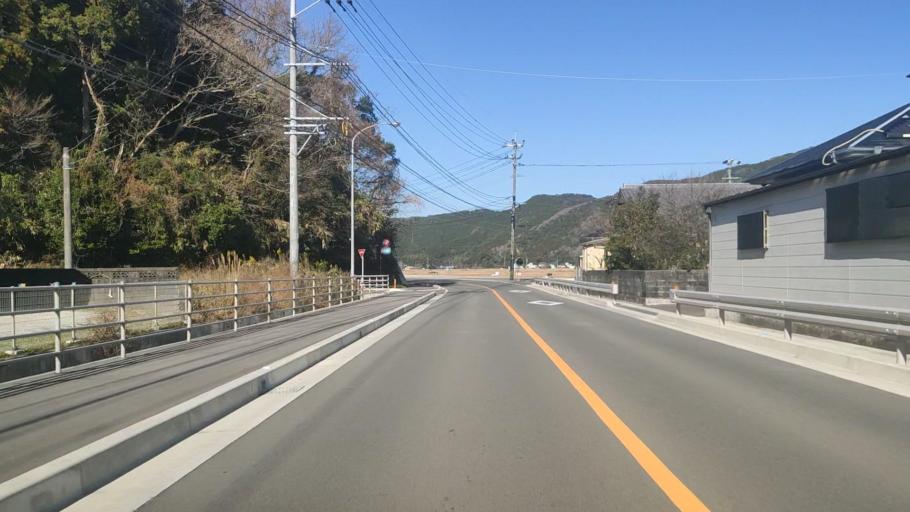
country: JP
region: Oita
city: Saiki
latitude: 32.9237
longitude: 131.9263
